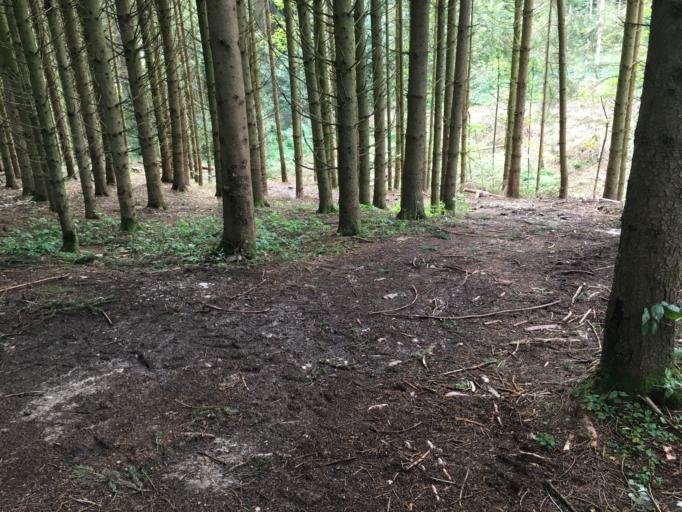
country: AT
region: Upper Austria
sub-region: Politischer Bezirk Vocklabruck
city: Pfaffing
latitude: 48.0068
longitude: 13.4629
